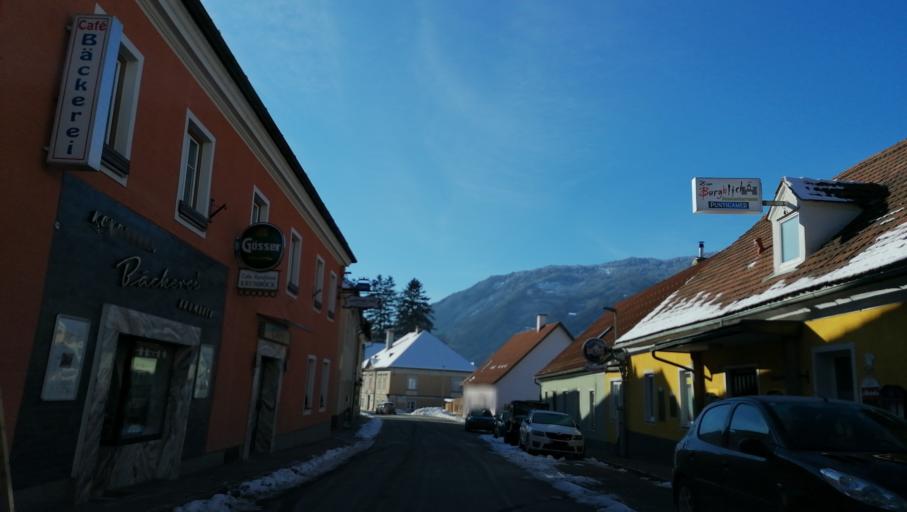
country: AT
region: Styria
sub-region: Politischer Bezirk Murtal
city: Sankt Georgen ob Judenburg
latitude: 47.1985
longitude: 14.4447
